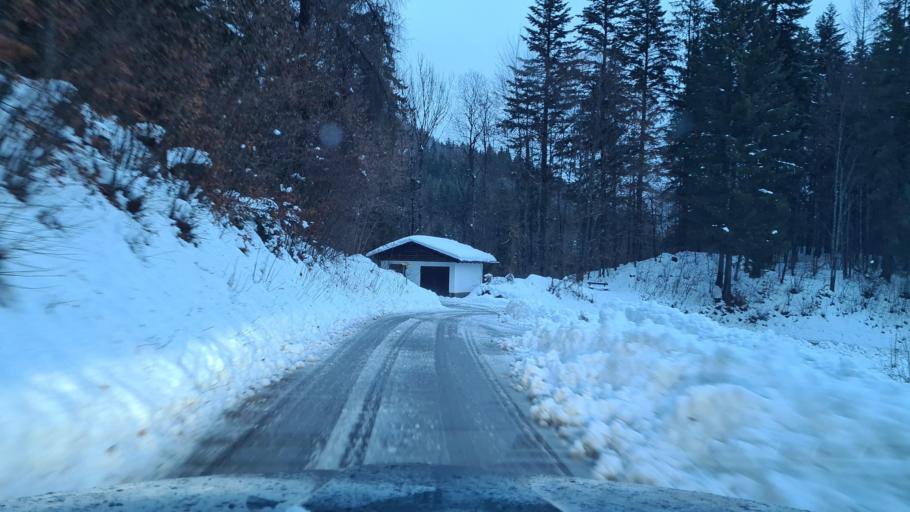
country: AT
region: Salzburg
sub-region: Politischer Bezirk Sankt Johann im Pongau
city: Werfen
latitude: 47.4892
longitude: 13.1580
